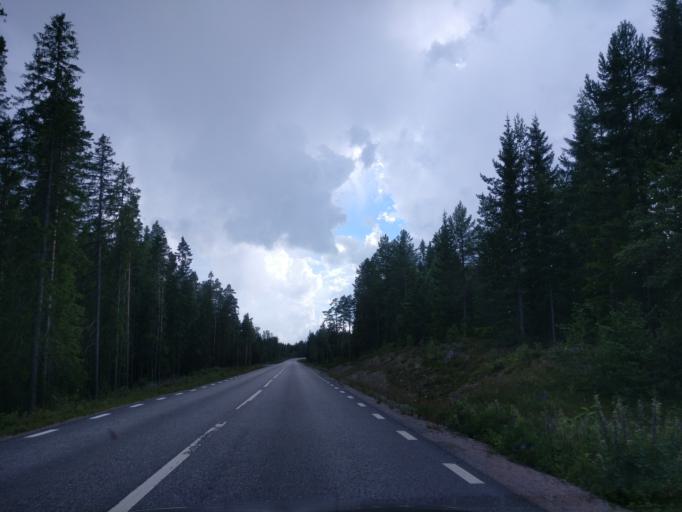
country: SE
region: Dalarna
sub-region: Ludvika Kommun
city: Abborrberget
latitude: 60.1739
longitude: 14.6667
